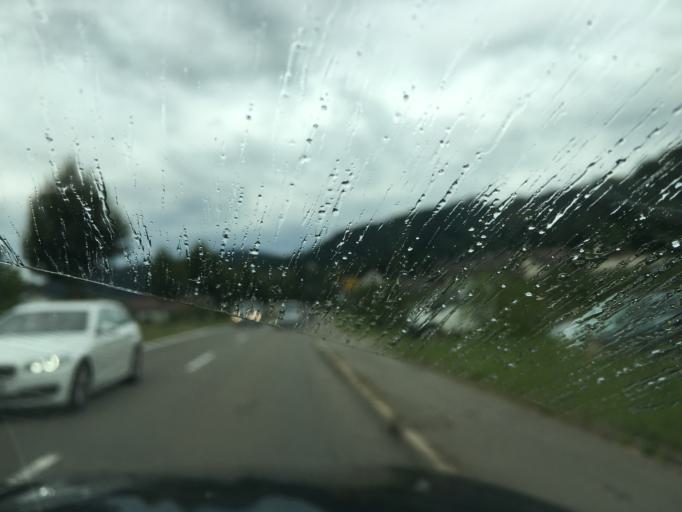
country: DE
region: Baden-Wuerttemberg
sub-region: Tuebingen Region
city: Rot
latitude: 47.8612
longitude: 9.0999
